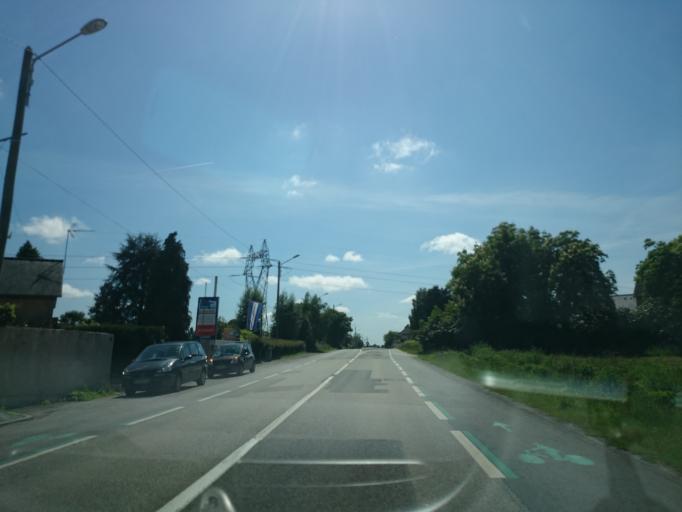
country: FR
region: Brittany
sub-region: Departement d'Ille-et-Vilaine
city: Cesson-Sevigne
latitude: 48.1474
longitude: -1.6053
